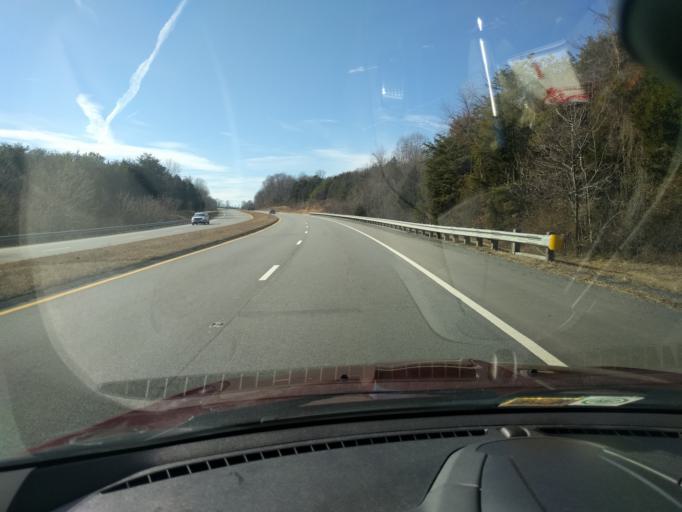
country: US
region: Virginia
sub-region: Amherst County
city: Madison Heights
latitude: 37.4689
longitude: -79.0979
